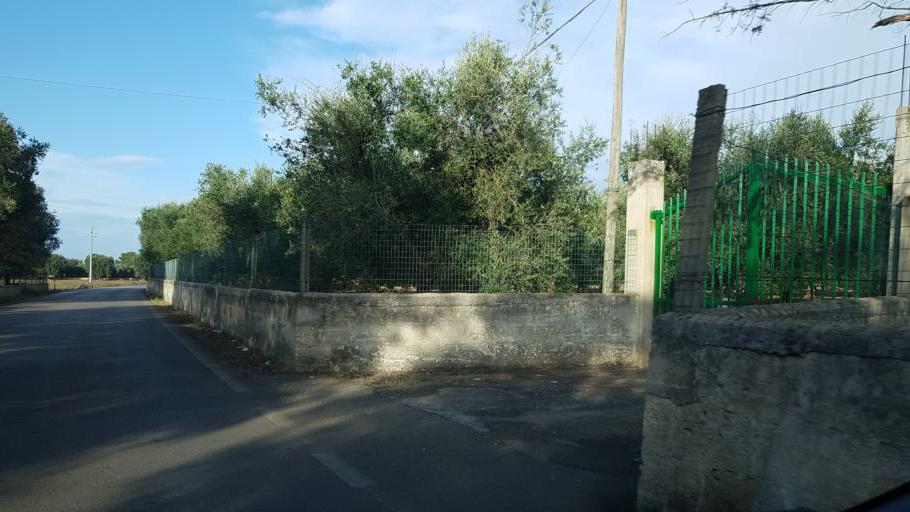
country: IT
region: Apulia
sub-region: Provincia di Brindisi
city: Oria
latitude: 40.5126
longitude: 17.6498
